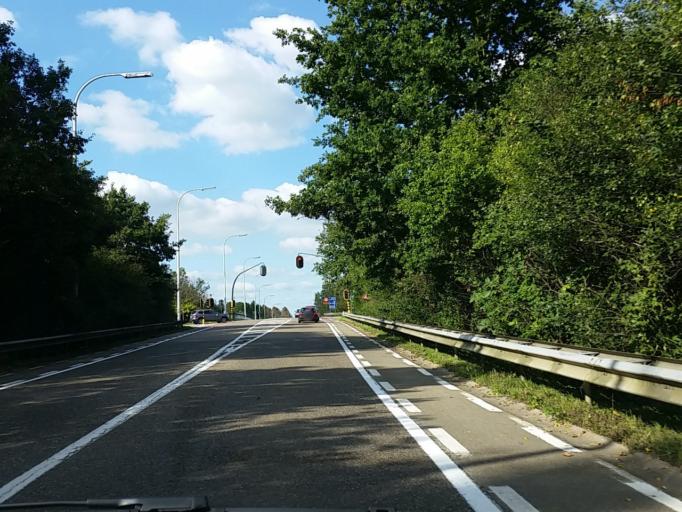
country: BE
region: Flanders
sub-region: Provincie Vlaams-Brabant
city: Holsbeek
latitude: 50.9311
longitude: 4.7450
